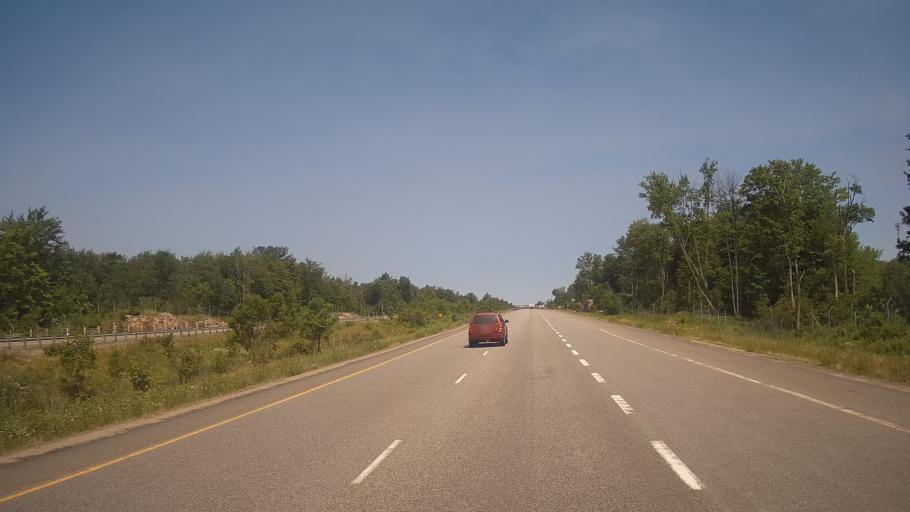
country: CA
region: Ontario
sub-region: Parry Sound District
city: Parry Sound
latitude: 45.0956
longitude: -79.7857
